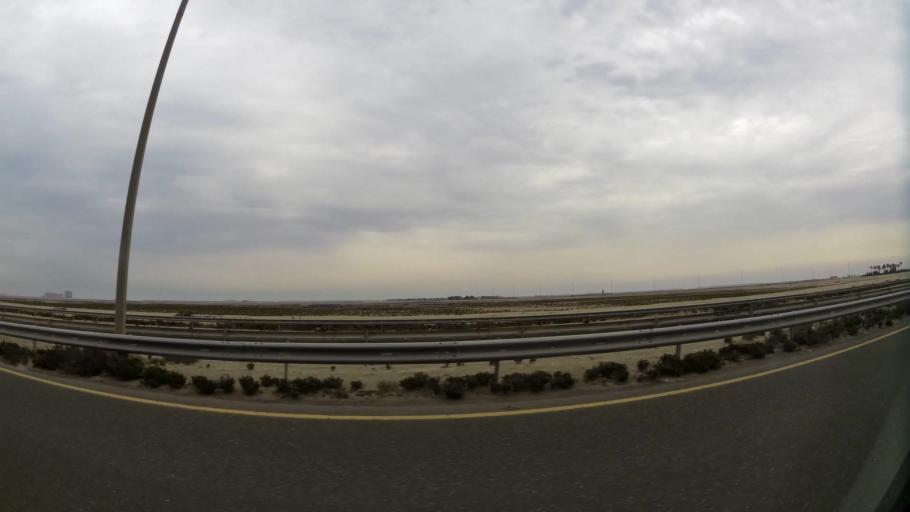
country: BH
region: Central Governorate
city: Dar Kulayb
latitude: 25.8504
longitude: 50.5834
